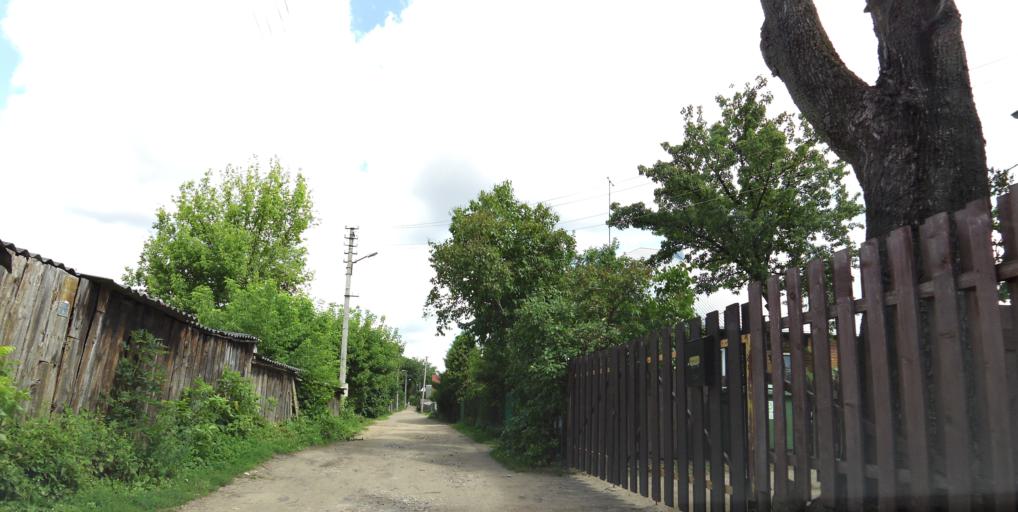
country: LT
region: Vilnius County
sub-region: Vilnius
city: Vilnius
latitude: 54.7005
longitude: 25.2802
